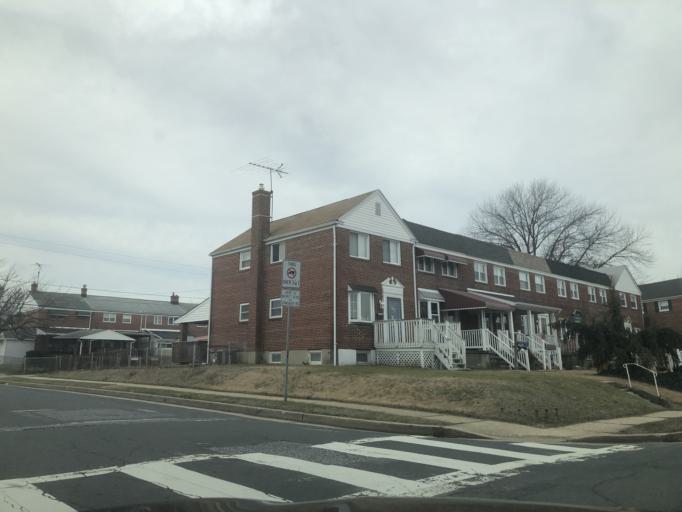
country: US
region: Maryland
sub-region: Baltimore County
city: Dundalk
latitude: 39.2638
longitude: -76.5044
